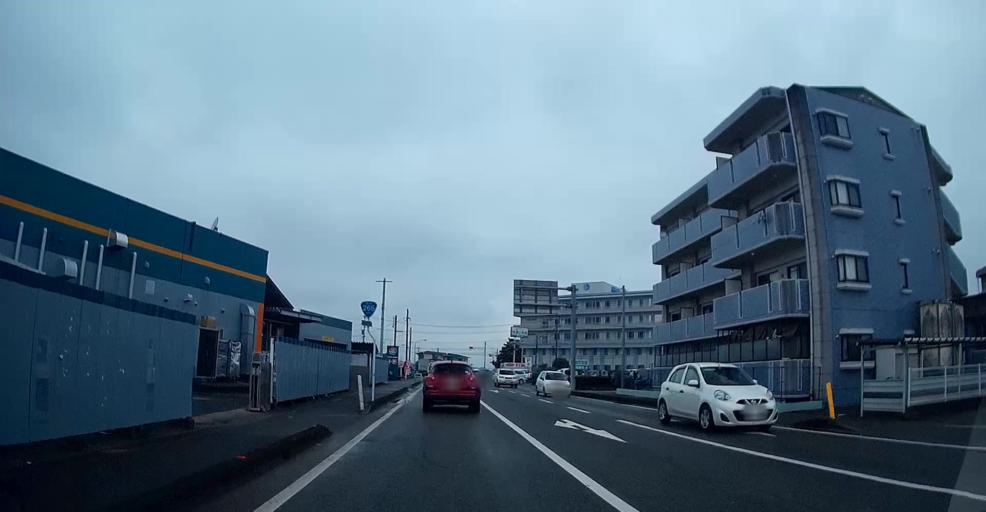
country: JP
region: Kumamoto
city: Kumamoto
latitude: 32.7488
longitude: 130.7395
